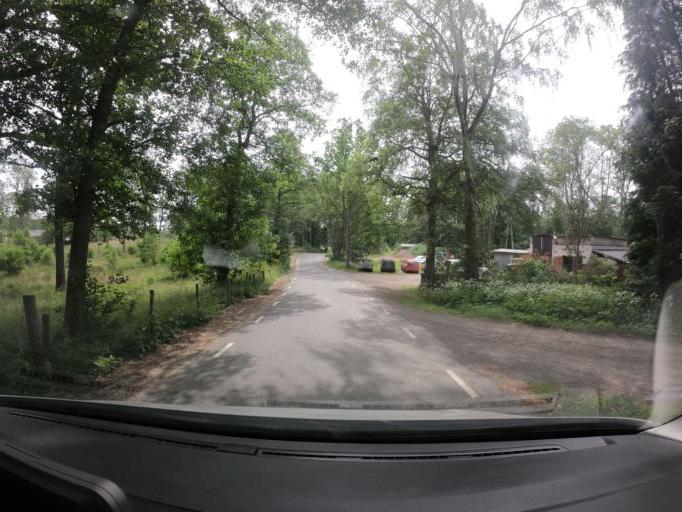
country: SE
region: Skane
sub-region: Hassleholms Kommun
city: Sosdala
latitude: 56.0068
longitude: 13.6147
